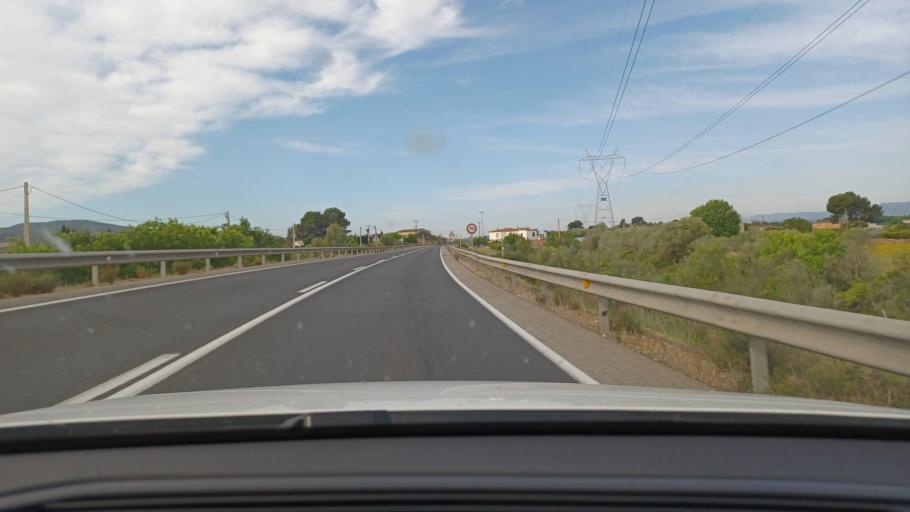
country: ES
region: Catalonia
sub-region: Provincia de Tarragona
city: Santa Barbara
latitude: 40.7091
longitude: 0.5060
